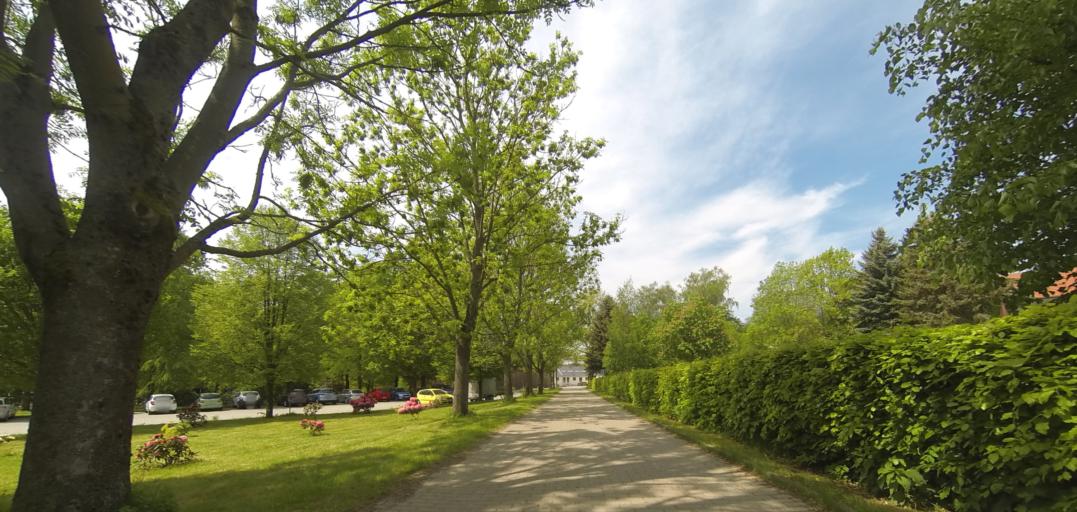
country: DE
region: Saxony
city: Grossharthau
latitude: 51.1074
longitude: 14.1089
